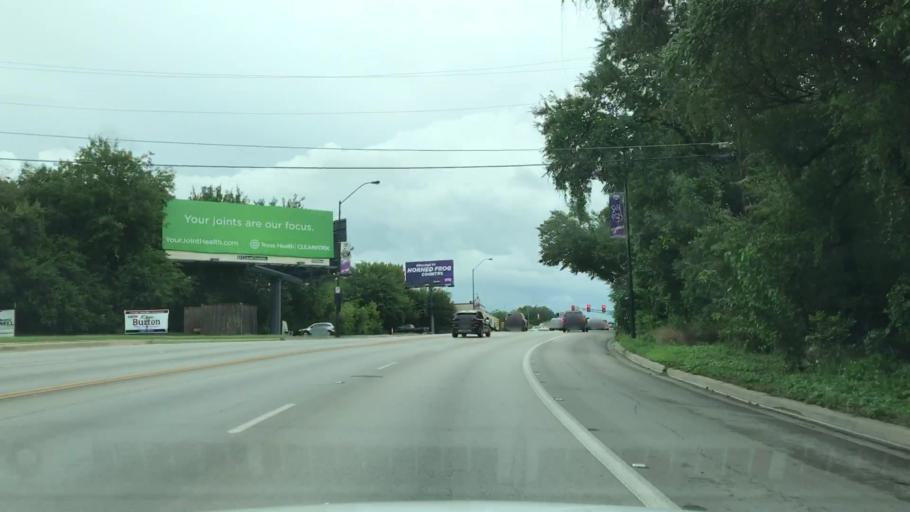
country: US
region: Texas
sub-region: Tarrant County
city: Fort Worth
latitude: 32.7176
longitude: -97.3605
